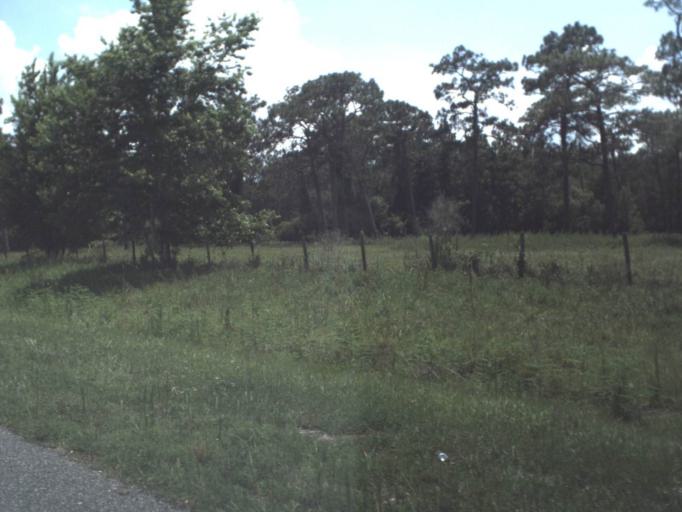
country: US
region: Florida
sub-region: Putnam County
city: East Palatka
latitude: 29.7521
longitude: -81.6415
